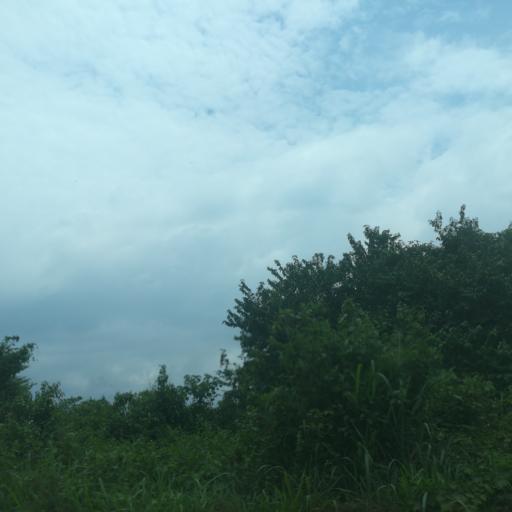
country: NG
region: Lagos
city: Ejirin
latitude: 6.6707
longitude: 3.7979
